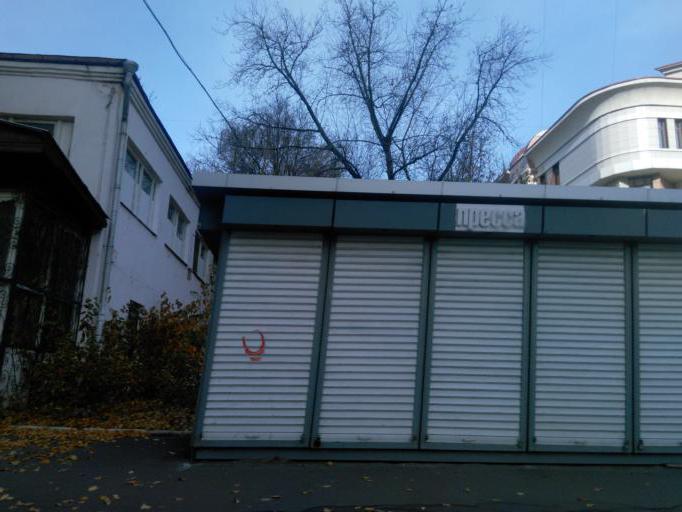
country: RU
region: Moscow
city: Ostankinskiy
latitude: 55.8240
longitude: 37.6268
